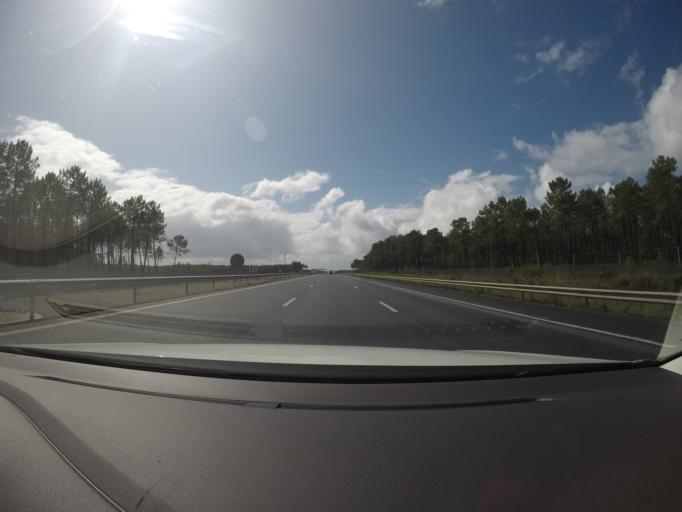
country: FR
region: Aquitaine
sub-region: Departement des Landes
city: Magescq
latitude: 43.8295
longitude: -1.1842
